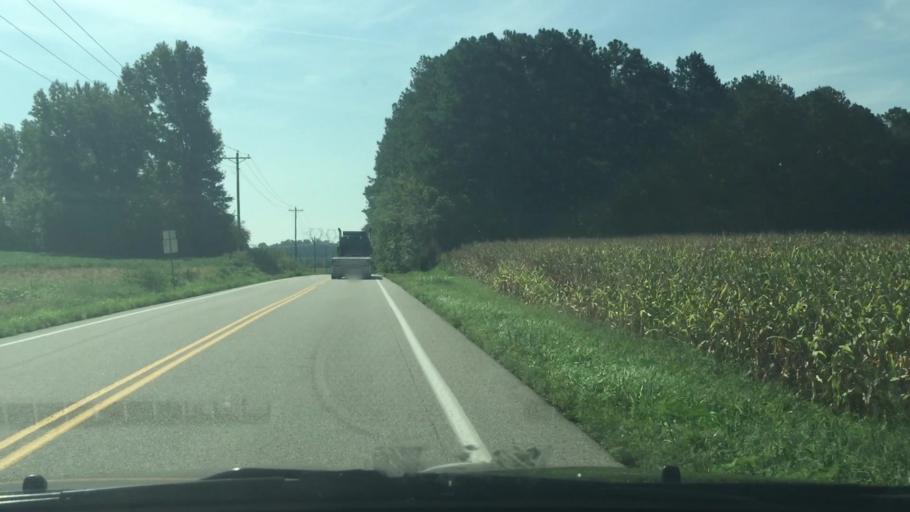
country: US
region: Virginia
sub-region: Sussex County
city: Sussex
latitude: 37.0645
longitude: -77.3337
